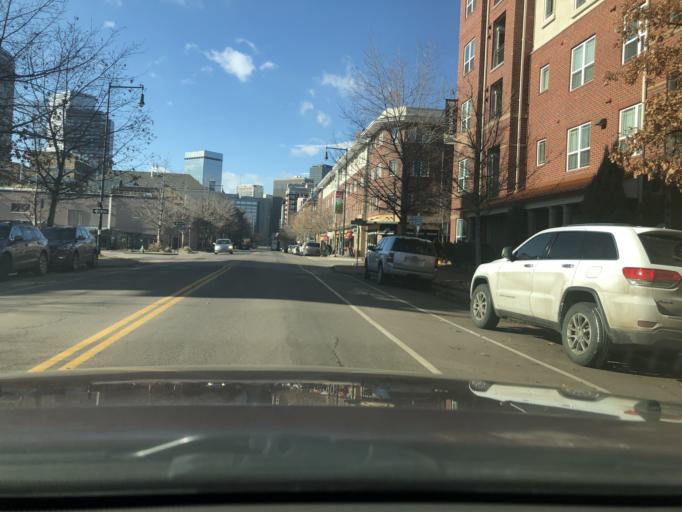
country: US
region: Colorado
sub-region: Denver County
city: Denver
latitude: 39.7462
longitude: -104.9782
